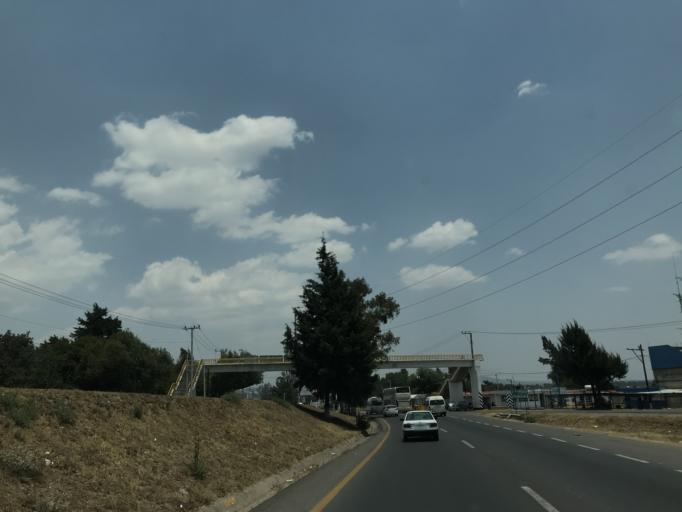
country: MX
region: Tlaxcala
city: Yauhquemehcan
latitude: 19.3947
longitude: -98.1758
